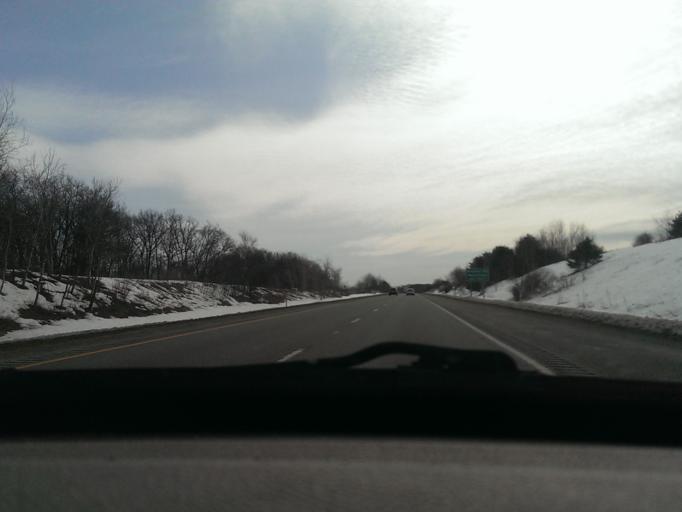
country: US
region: Massachusetts
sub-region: Worcester County
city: Whitinsville
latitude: 42.1114
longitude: -71.7054
